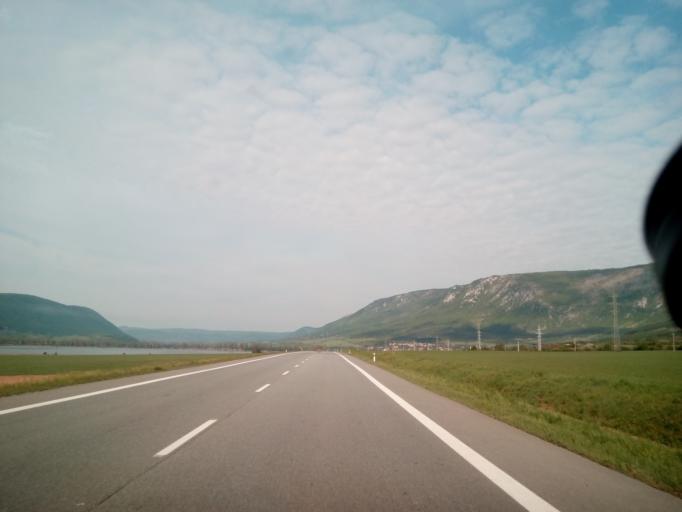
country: SK
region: Kosicky
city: Medzev
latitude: 48.6004
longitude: 20.7832
